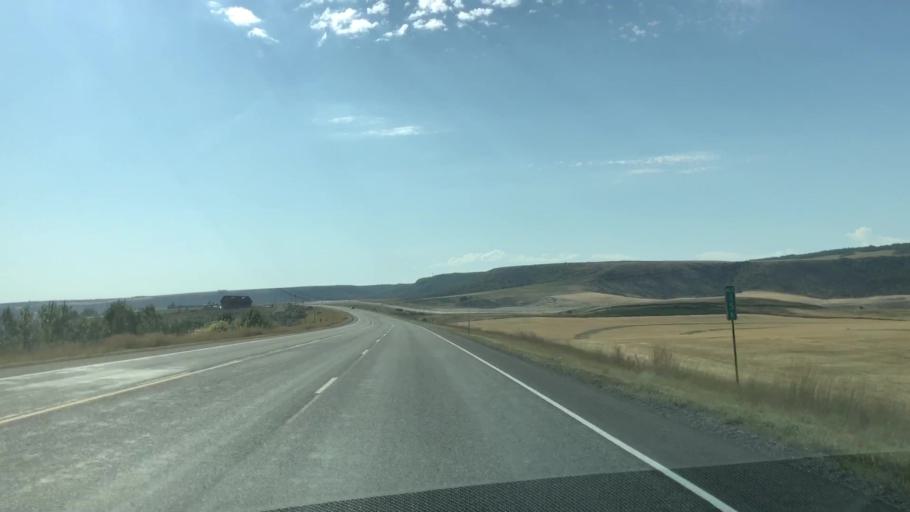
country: US
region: Idaho
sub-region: Madison County
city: Rexburg
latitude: 43.5978
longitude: -111.6470
